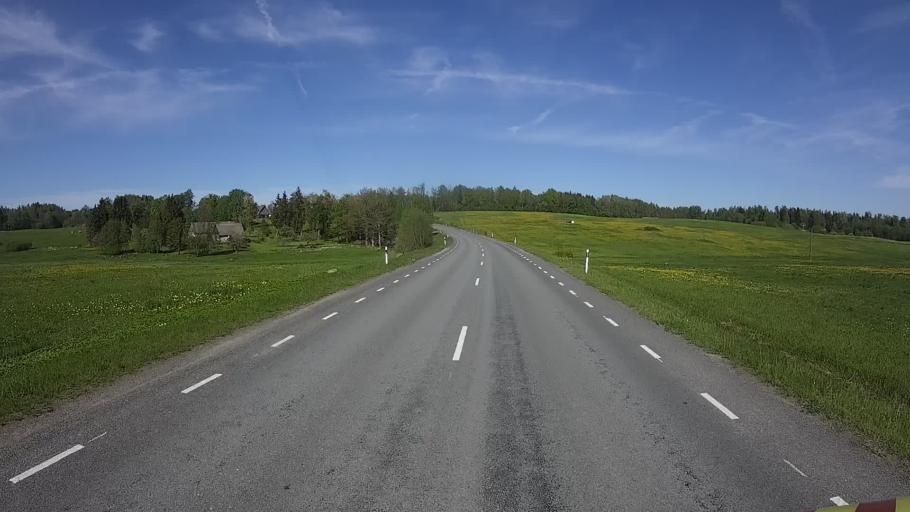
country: EE
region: Vorumaa
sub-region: Antsla vald
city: Vana-Antsla
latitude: 57.9522
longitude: 26.4396
